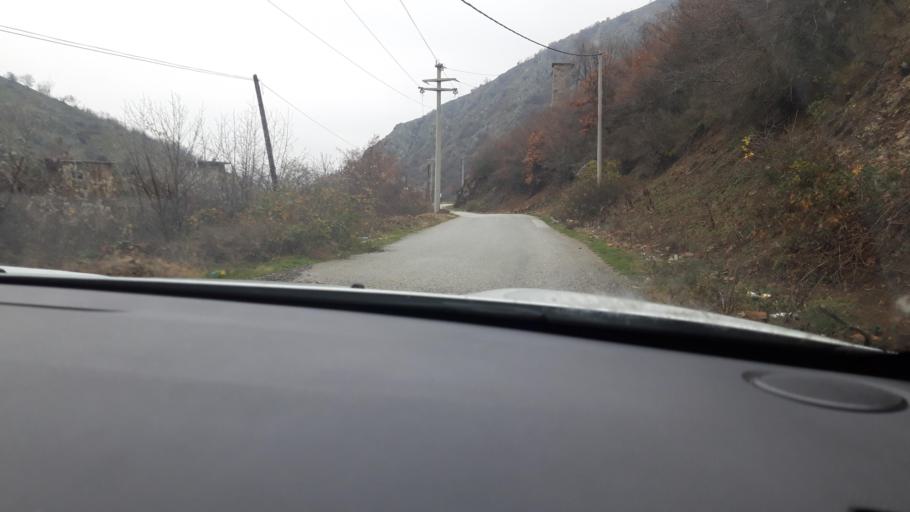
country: MK
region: Opstina Lipkovo
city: Lipkovo
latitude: 42.1663
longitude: 21.5724
